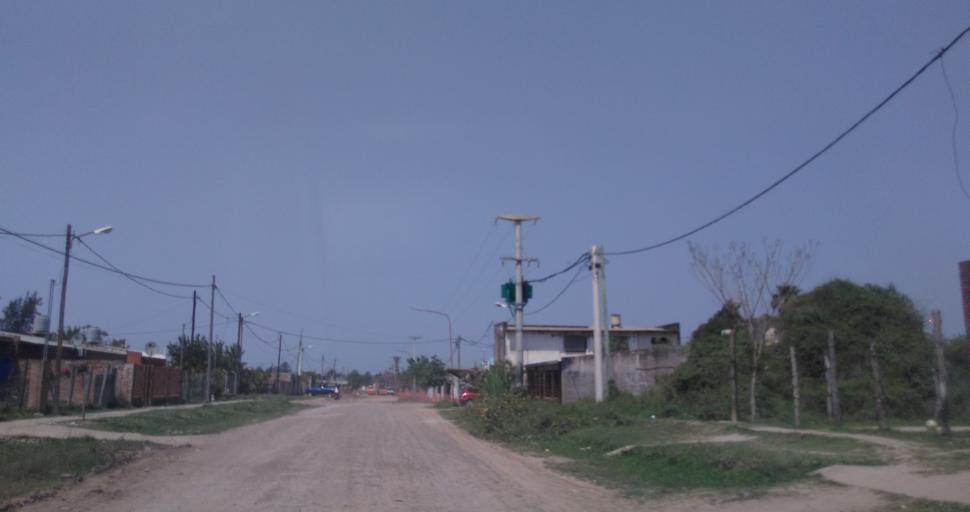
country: AR
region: Chaco
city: Fontana
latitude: -27.4219
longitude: -59.0268
